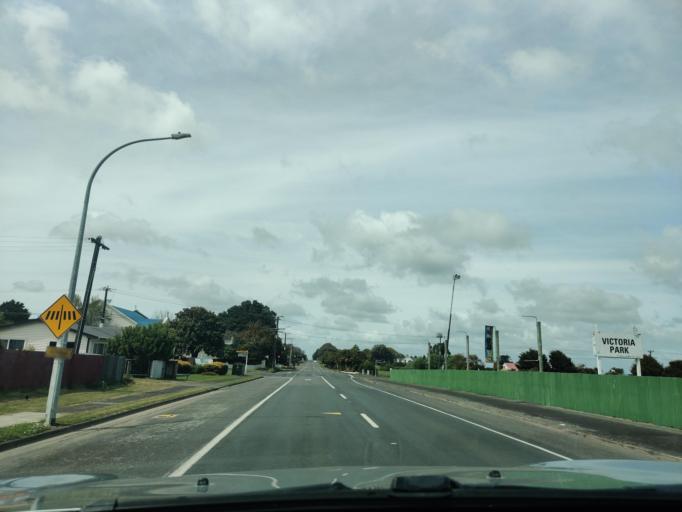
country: NZ
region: Taranaki
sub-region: South Taranaki District
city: Eltham
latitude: -39.4290
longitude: 174.1522
